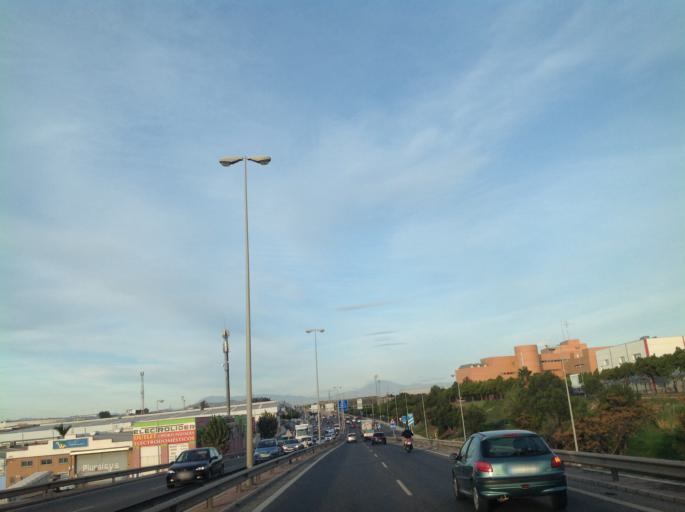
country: ES
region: Andalusia
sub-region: Provincia de Malaga
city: Malaga
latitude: 36.7137
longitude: -4.4740
